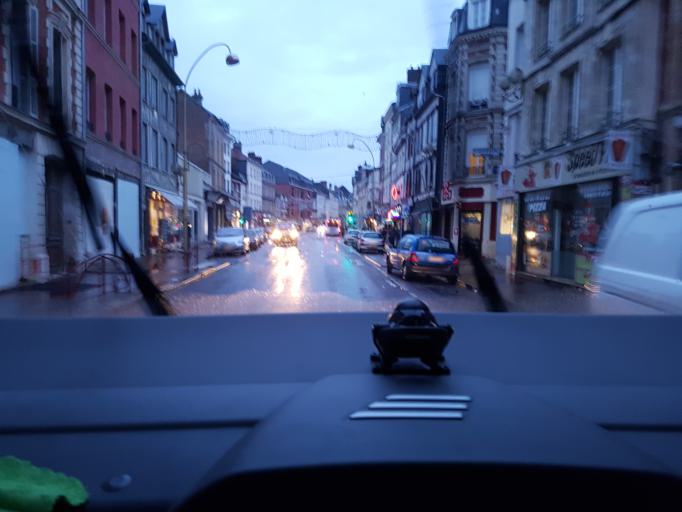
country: FR
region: Haute-Normandie
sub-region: Departement de la Seine-Maritime
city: Elbeuf
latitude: 49.2906
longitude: 1.0019
